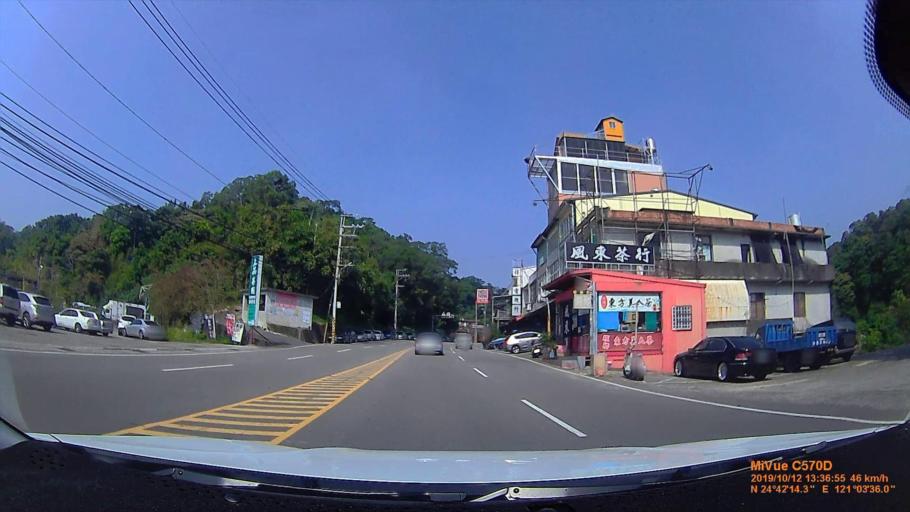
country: TW
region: Taiwan
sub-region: Hsinchu
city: Hsinchu
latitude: 24.7041
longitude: 121.0601
